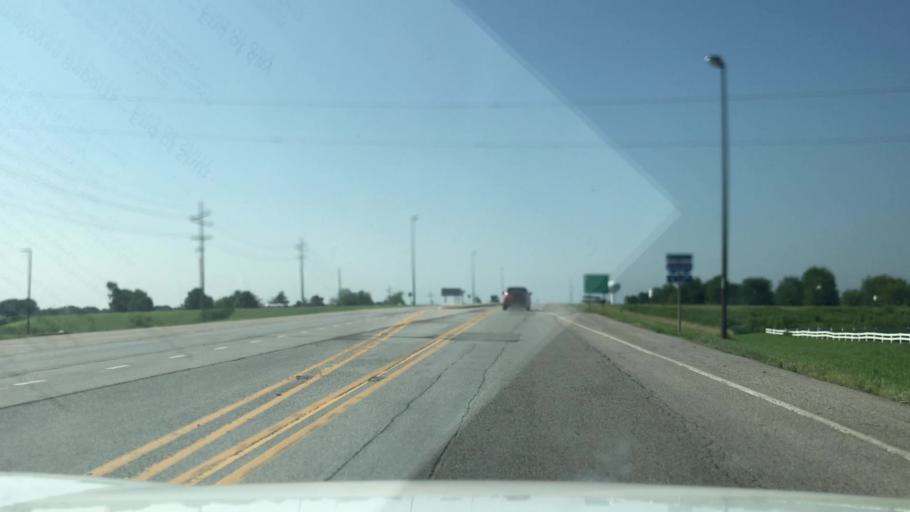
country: US
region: Illinois
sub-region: Saint Clair County
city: Scott Air Force Base
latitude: 38.5556
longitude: -89.8072
